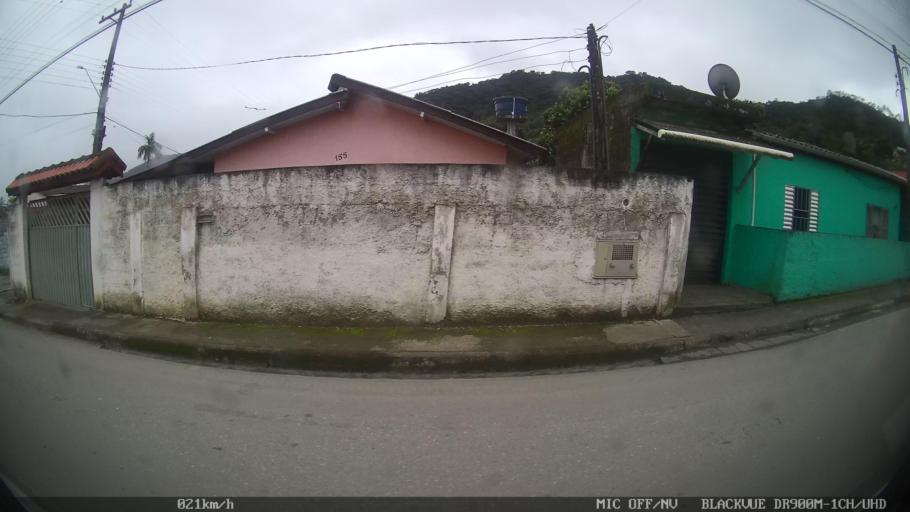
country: BR
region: Sao Paulo
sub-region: Juquia
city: Juquia
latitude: -24.3122
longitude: -47.6275
